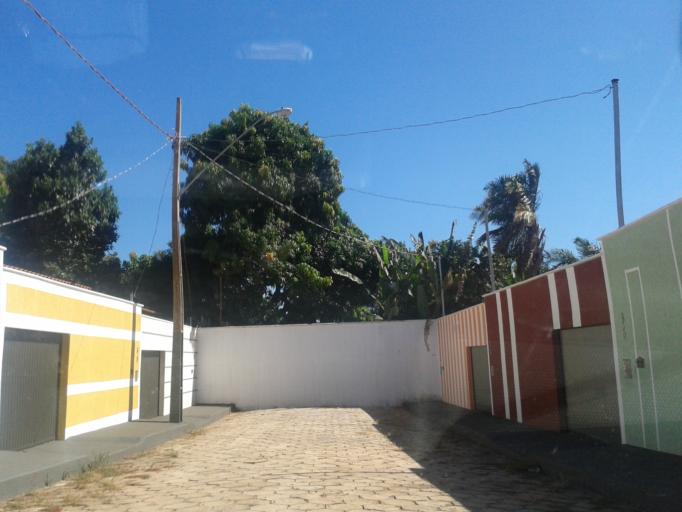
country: BR
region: Minas Gerais
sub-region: Santa Vitoria
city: Santa Vitoria
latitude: -18.6920
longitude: -49.9397
